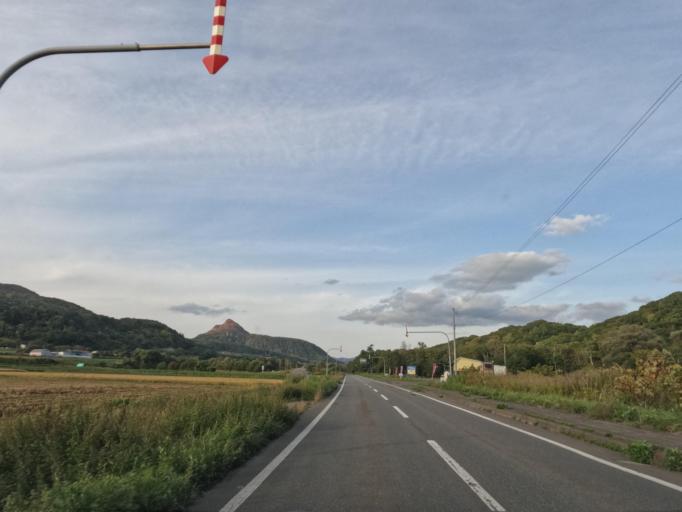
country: JP
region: Hokkaido
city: Date
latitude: 42.5118
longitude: 140.8630
